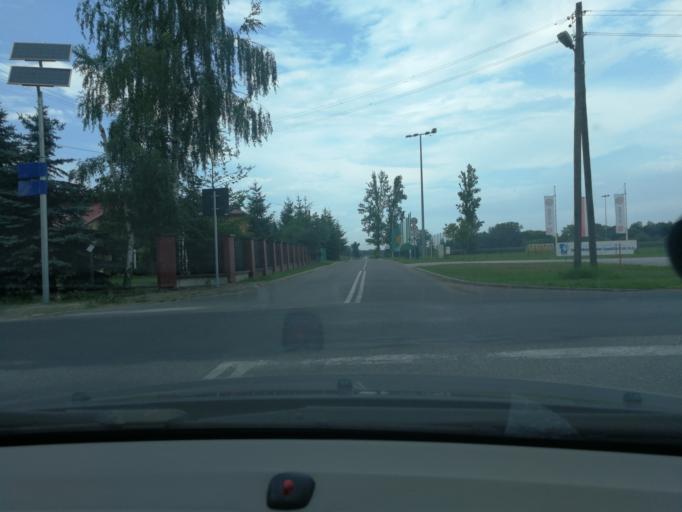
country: PL
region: Masovian Voivodeship
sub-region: Powiat grodziski
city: Grodzisk Mazowiecki
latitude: 52.1317
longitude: 20.5877
